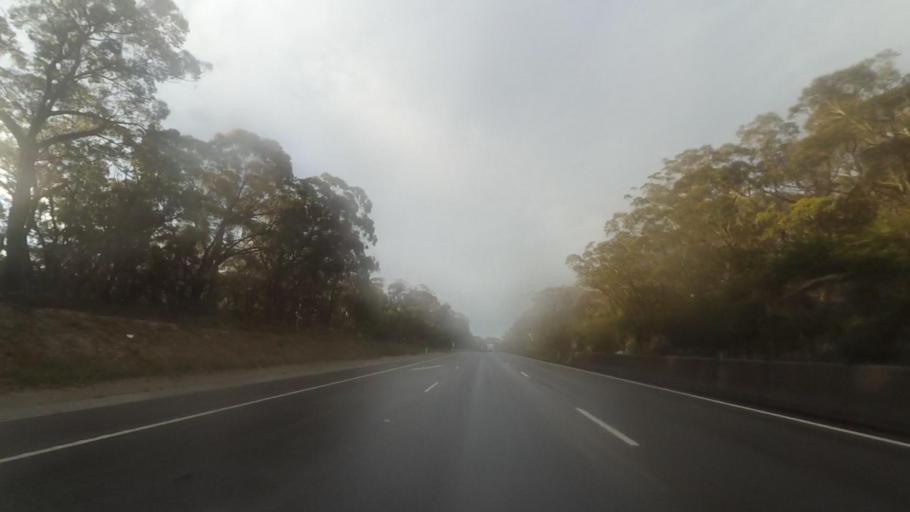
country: AU
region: New South Wales
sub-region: Wollongong
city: Mount Ousley
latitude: -34.3611
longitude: 150.8582
